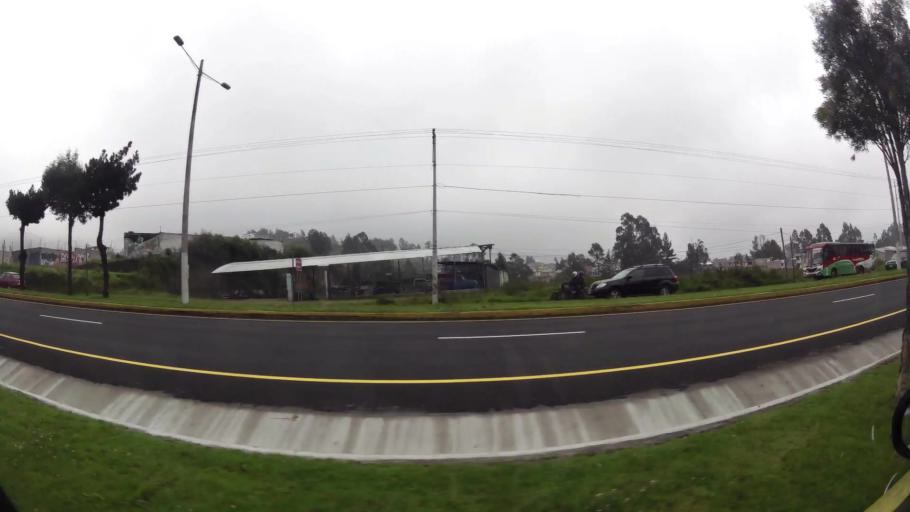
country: EC
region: Pichincha
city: Quito
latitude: -0.2775
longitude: -78.4846
